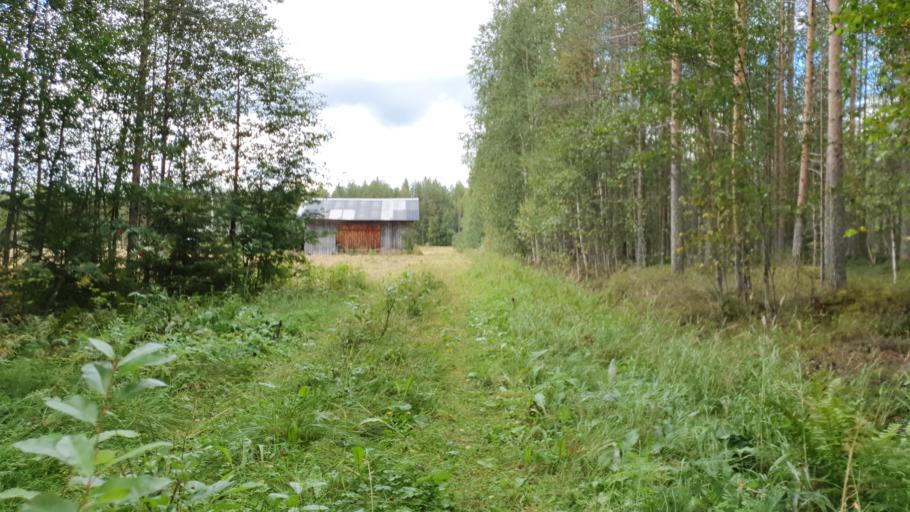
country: FI
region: Kainuu
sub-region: Kehys-Kainuu
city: Kuhmo
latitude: 64.1342
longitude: 29.4521
